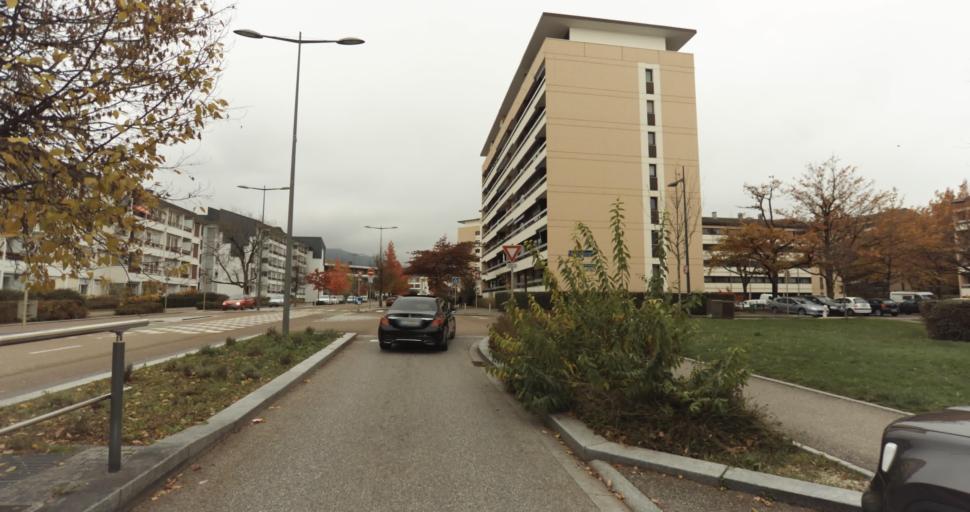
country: FR
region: Rhone-Alpes
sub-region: Departement de la Haute-Savoie
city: Cran-Gevrier
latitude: 45.8907
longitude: 6.1013
